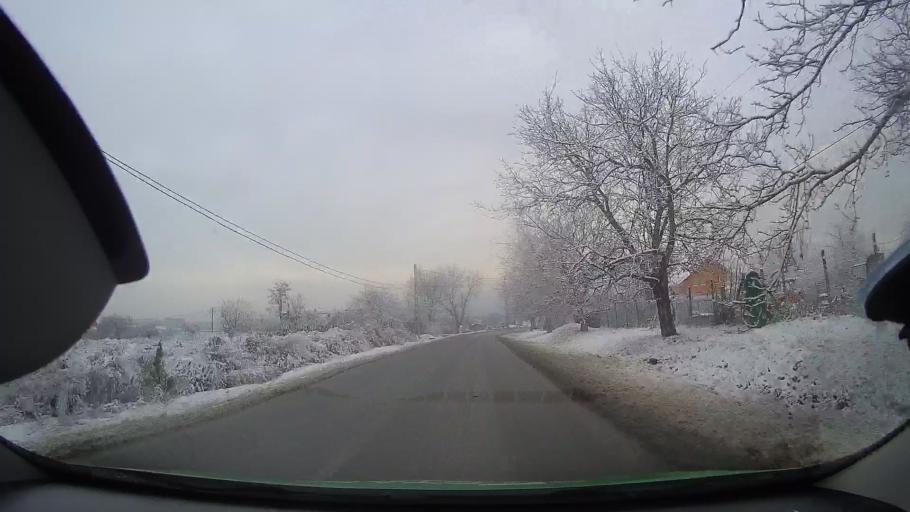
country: RO
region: Mures
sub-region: Comuna Bogata
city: Bogata
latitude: 46.4590
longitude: 24.0797
